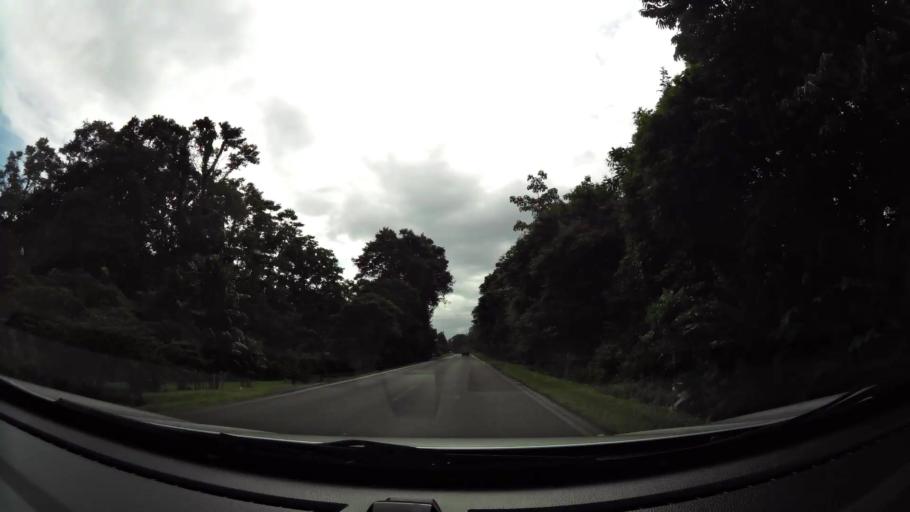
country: CR
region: Limon
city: Pocora
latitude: 10.1843
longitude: -83.6290
